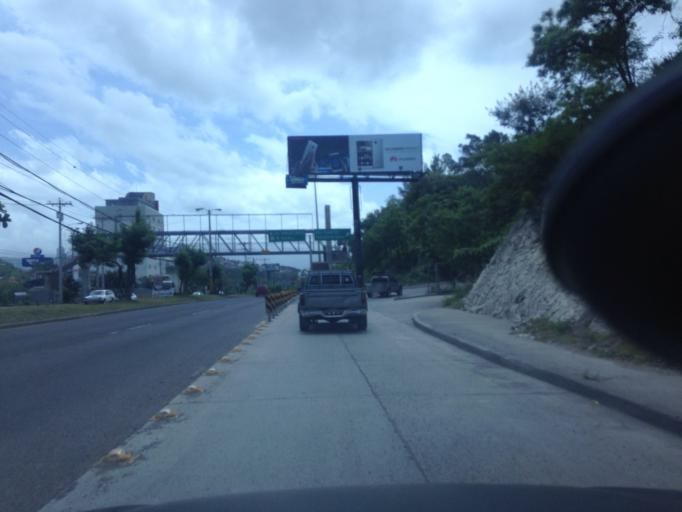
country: HN
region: Francisco Morazan
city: Tegucigalpa
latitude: 14.0743
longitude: -87.2012
